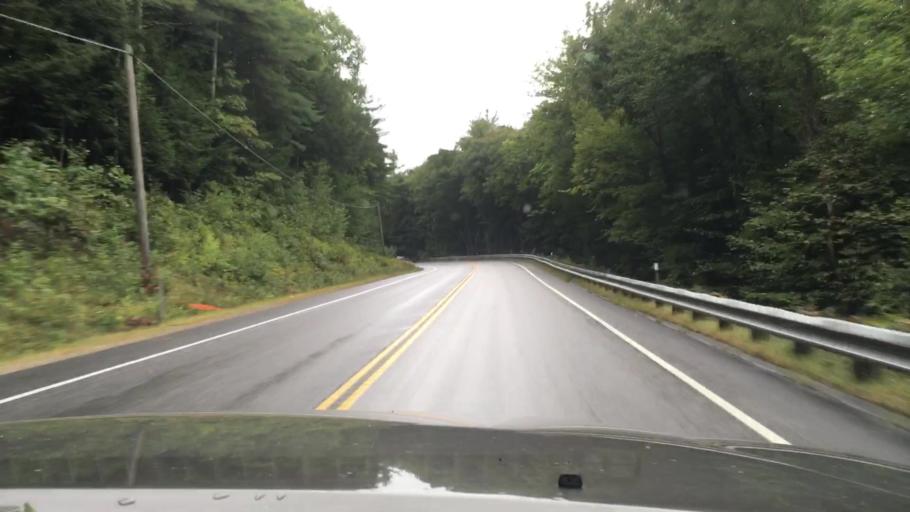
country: US
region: New Hampshire
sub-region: Hillsborough County
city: Antrim
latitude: 43.0764
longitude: -71.9857
